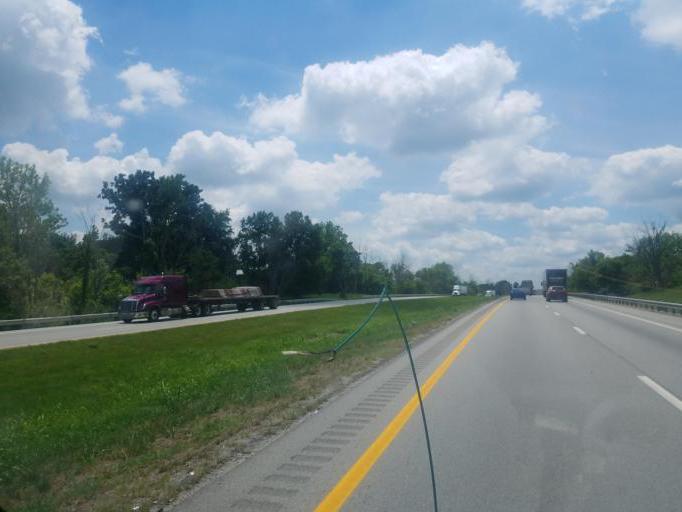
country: US
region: Kentucky
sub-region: Trimble County
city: Providence
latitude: 38.5767
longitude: -85.1814
